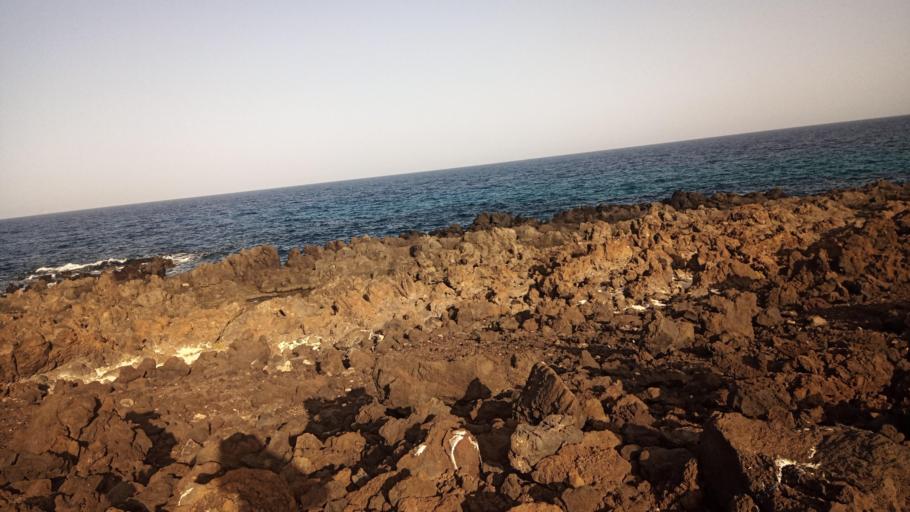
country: ES
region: Canary Islands
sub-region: Provincia de Las Palmas
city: Haria
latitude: 29.2080
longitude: -13.4240
